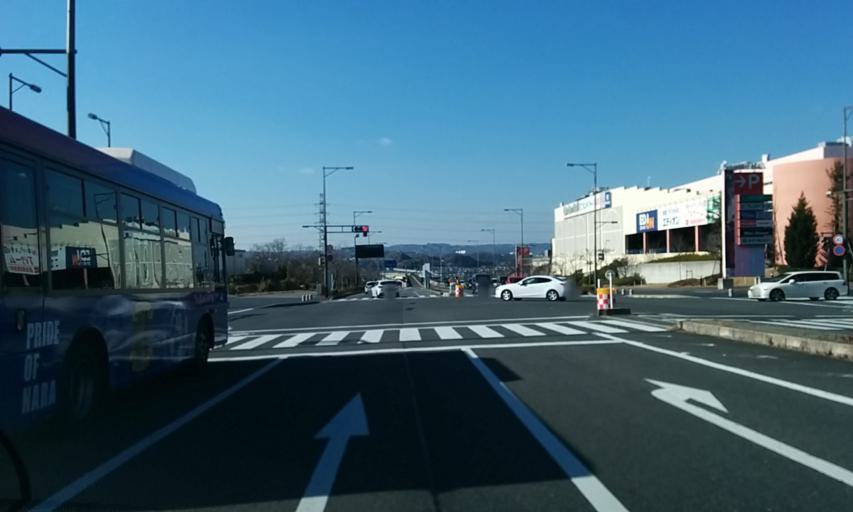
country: JP
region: Nara
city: Nara-shi
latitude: 34.7177
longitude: 135.8176
